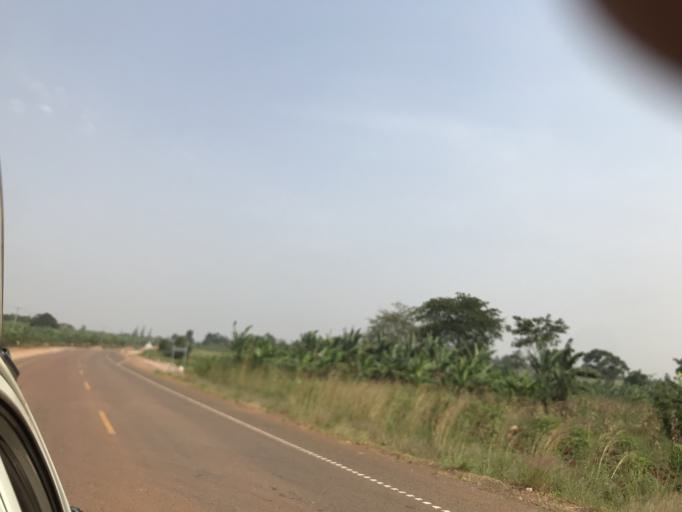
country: UG
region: Central Region
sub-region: Kalungu District
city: Kalungu
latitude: -0.2277
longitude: 31.7286
